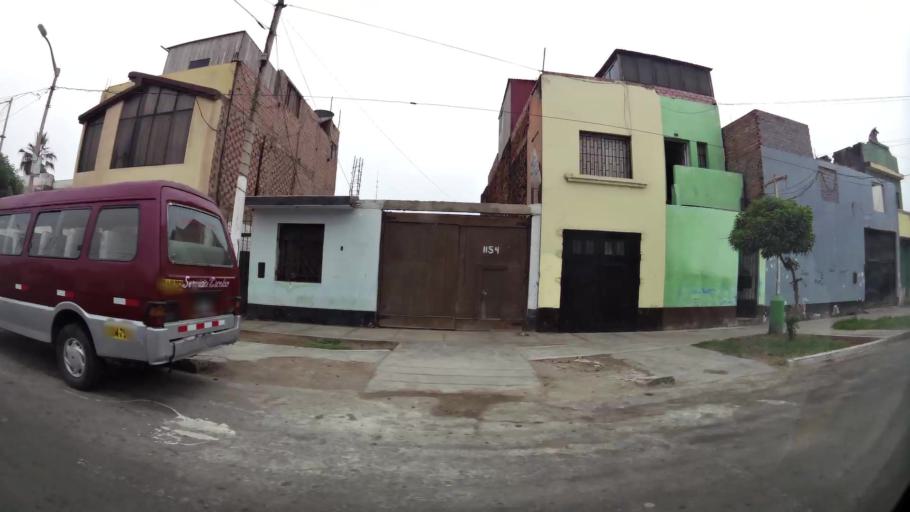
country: PE
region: Callao
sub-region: Callao
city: Callao
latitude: -12.0683
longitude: -77.1313
